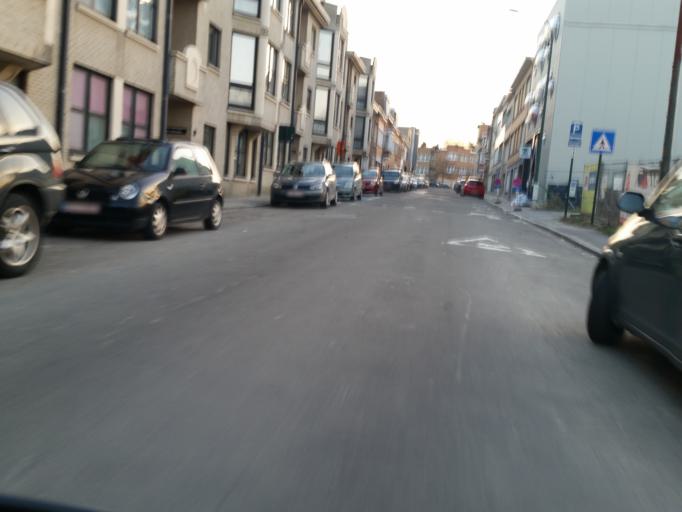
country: BE
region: Flanders
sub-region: Provincie Vlaams-Brabant
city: Grimbergen
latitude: 50.8950
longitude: 4.3750
